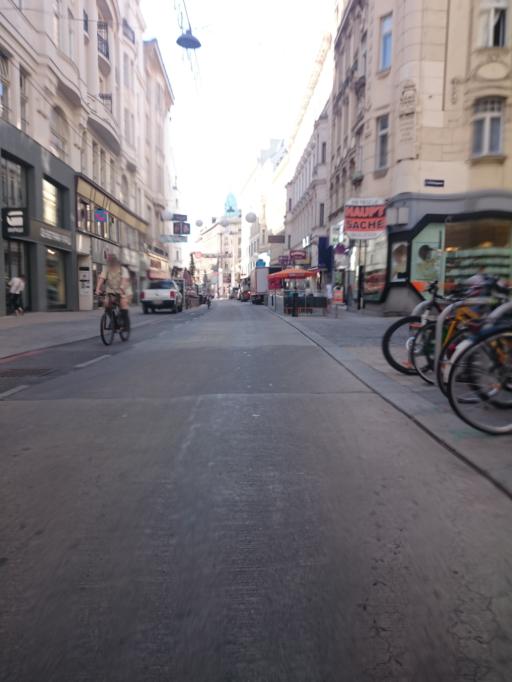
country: AT
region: Vienna
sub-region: Wien Stadt
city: Vienna
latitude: 48.1995
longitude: 16.3495
